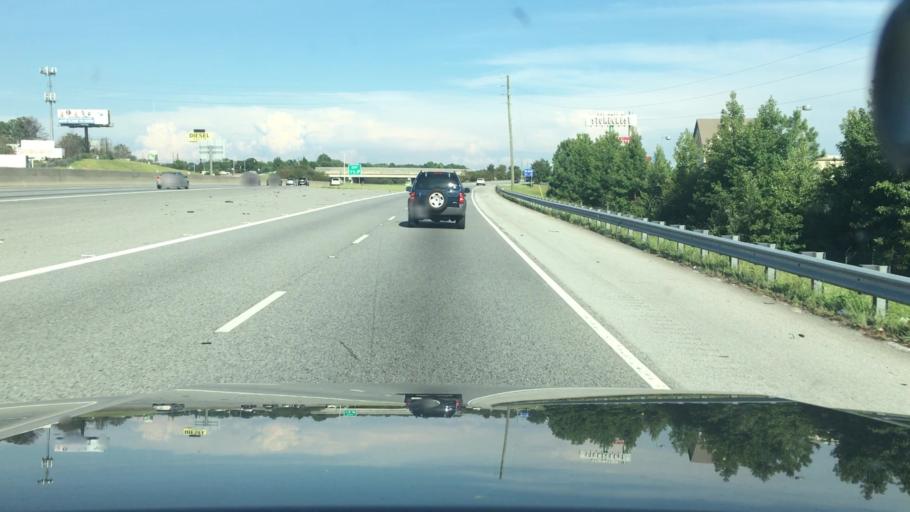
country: US
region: Georgia
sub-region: DeKalb County
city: Lithonia
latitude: 33.7014
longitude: -84.0935
